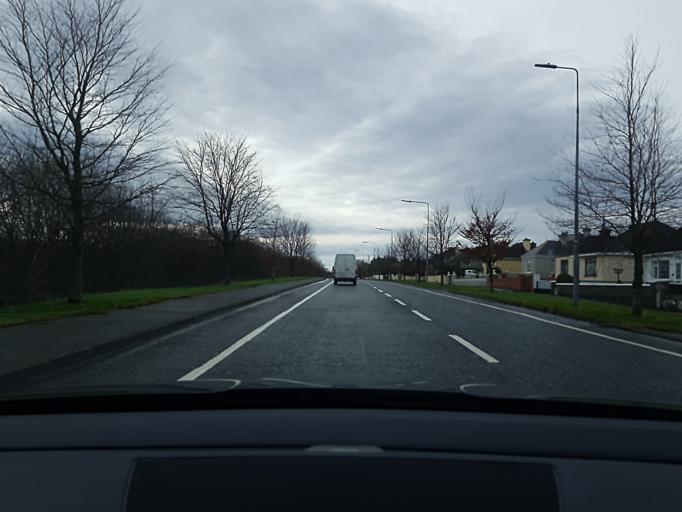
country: IE
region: Connaught
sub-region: Maigh Eo
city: Castlebar
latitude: 53.8434
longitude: -9.2902
